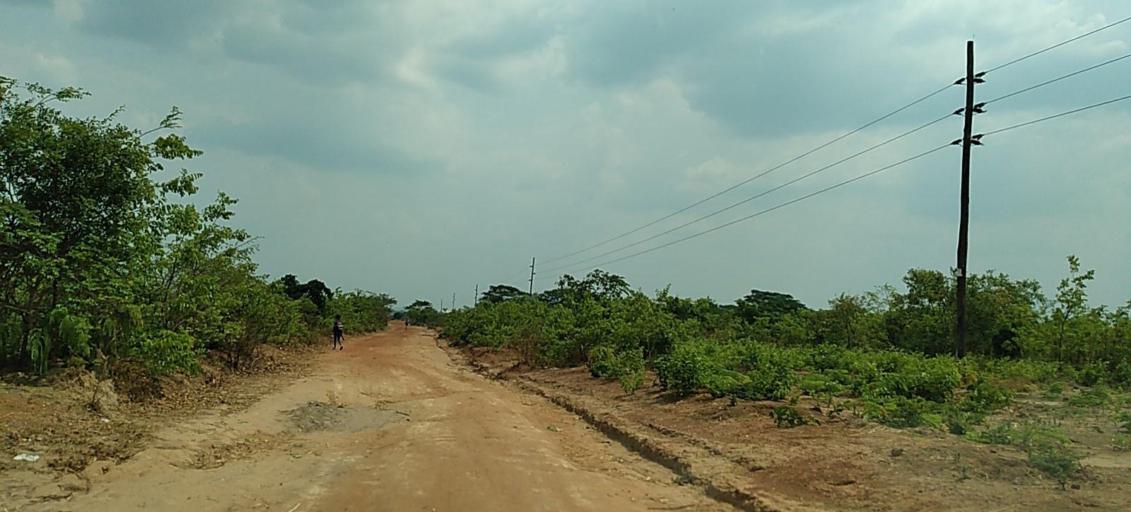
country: ZM
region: Copperbelt
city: Kalulushi
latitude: -12.8694
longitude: 28.0778
